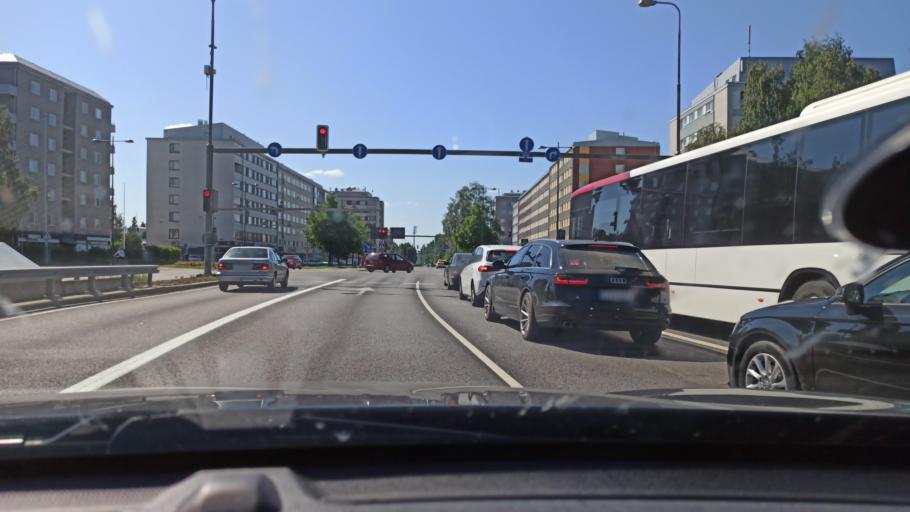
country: FI
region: Northern Ostrobothnia
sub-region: Oulu
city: Oulu
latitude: 65.0265
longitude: 25.4709
